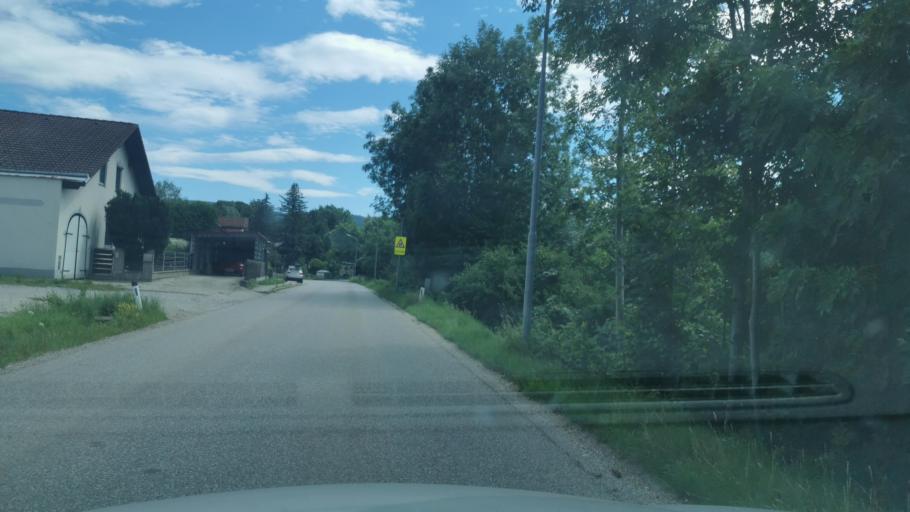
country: AT
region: Lower Austria
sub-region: Politischer Bezirk Sankt Polten
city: Pyhra
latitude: 48.1467
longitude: 15.6402
